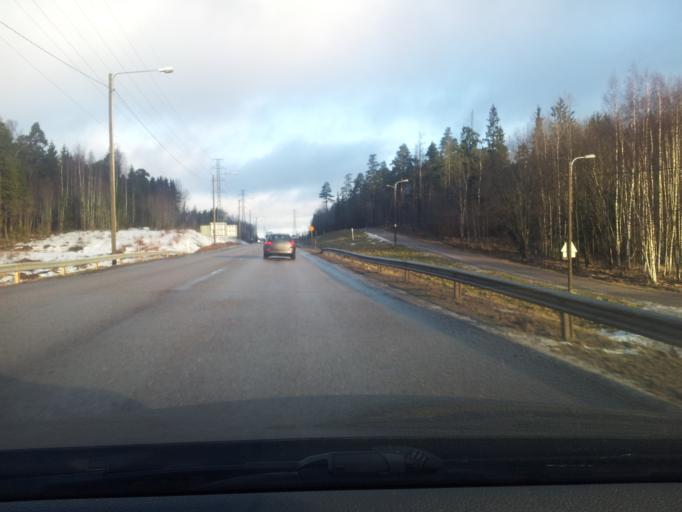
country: FI
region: Uusimaa
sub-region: Helsinki
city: Espoo
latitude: 60.1765
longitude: 24.6122
